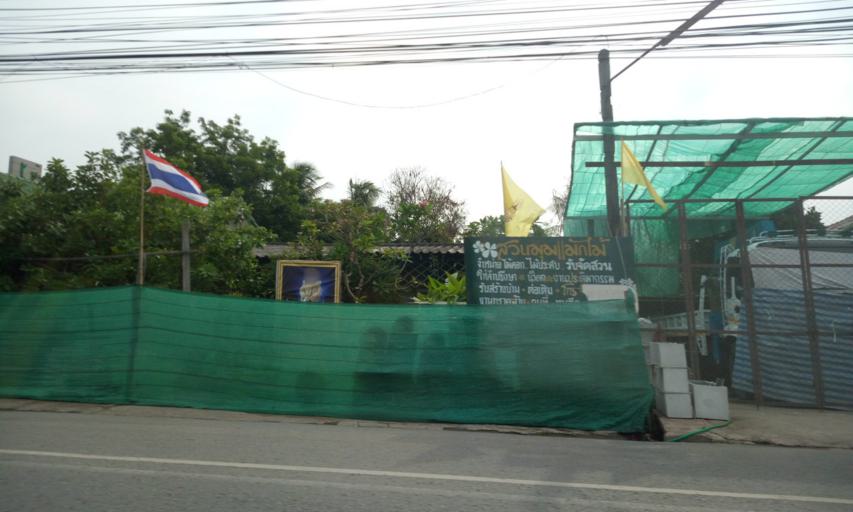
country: TH
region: Bangkok
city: Bang Na
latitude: 13.6889
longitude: 100.6991
